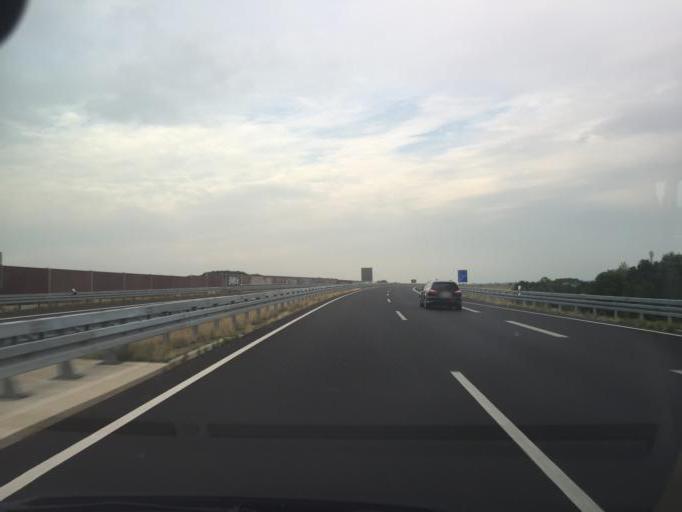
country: NL
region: Limburg
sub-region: Gemeente Venlo
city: Venlo
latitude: 51.3344
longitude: 6.1952
